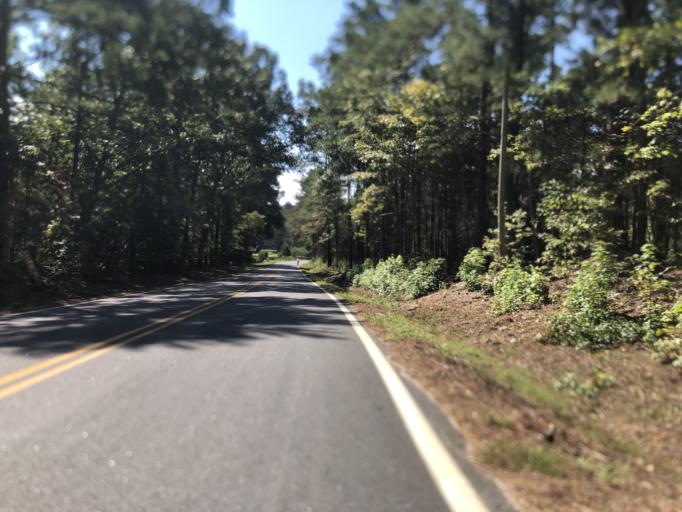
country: US
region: Georgia
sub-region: Heard County
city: Franklin
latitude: 33.3859
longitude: -84.9695
